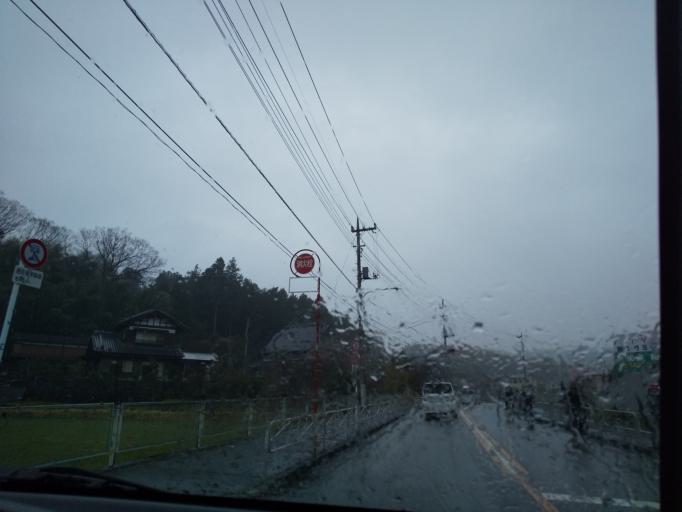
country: JP
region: Tokyo
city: Hino
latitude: 35.6347
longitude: 139.4058
